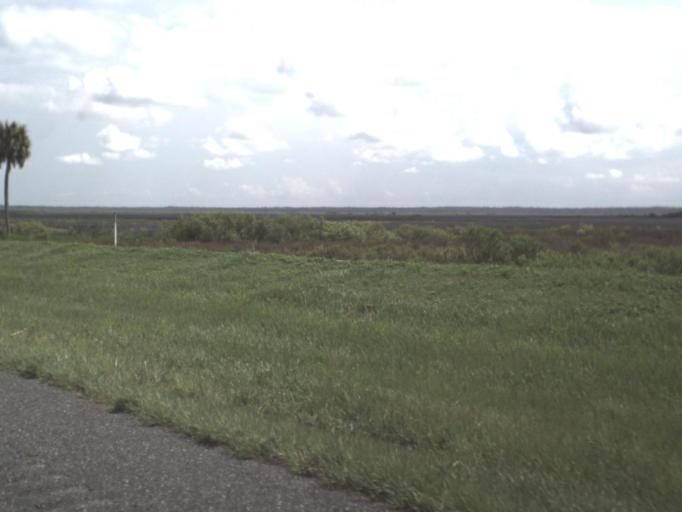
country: US
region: Florida
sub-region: Alachua County
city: Gainesville
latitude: 29.5616
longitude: -82.3319
